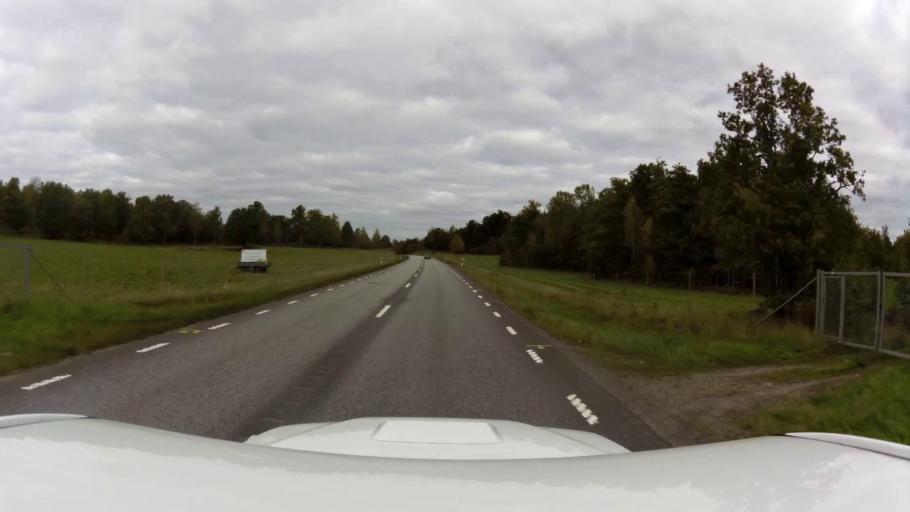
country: SE
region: OEstergoetland
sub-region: Kinda Kommun
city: Rimforsa
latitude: 58.2201
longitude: 15.6631
